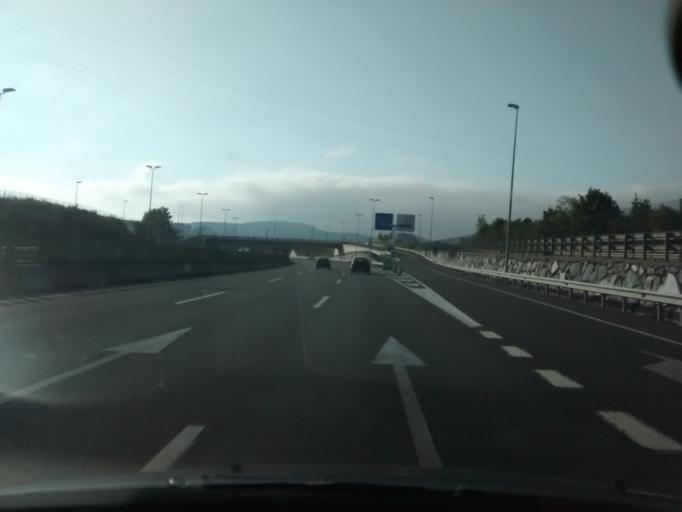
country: ES
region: Basque Country
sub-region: Bizkaia
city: Amorebieta
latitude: 43.2289
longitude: -2.7475
